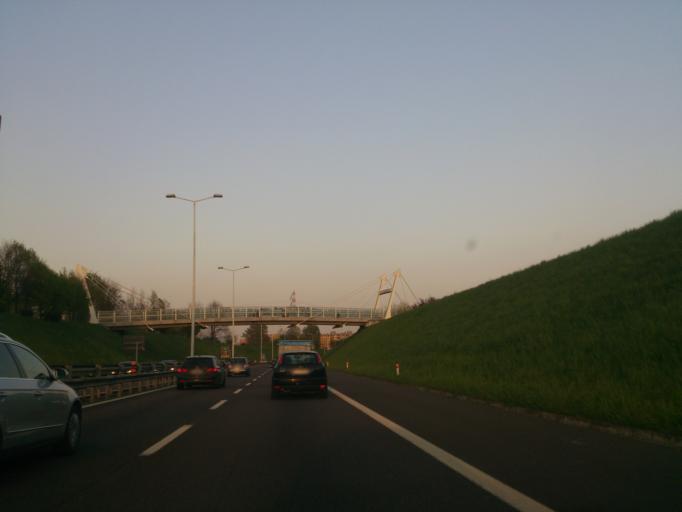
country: IT
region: Lombardy
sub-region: Provincia di Monza e Brianza
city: Muggio
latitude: 45.5766
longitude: 9.2138
